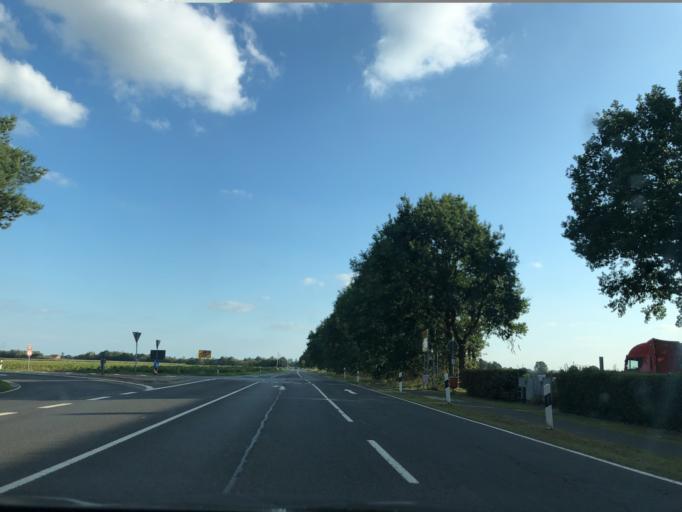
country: DE
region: Lower Saxony
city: Dersum
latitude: 52.9883
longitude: 7.2358
